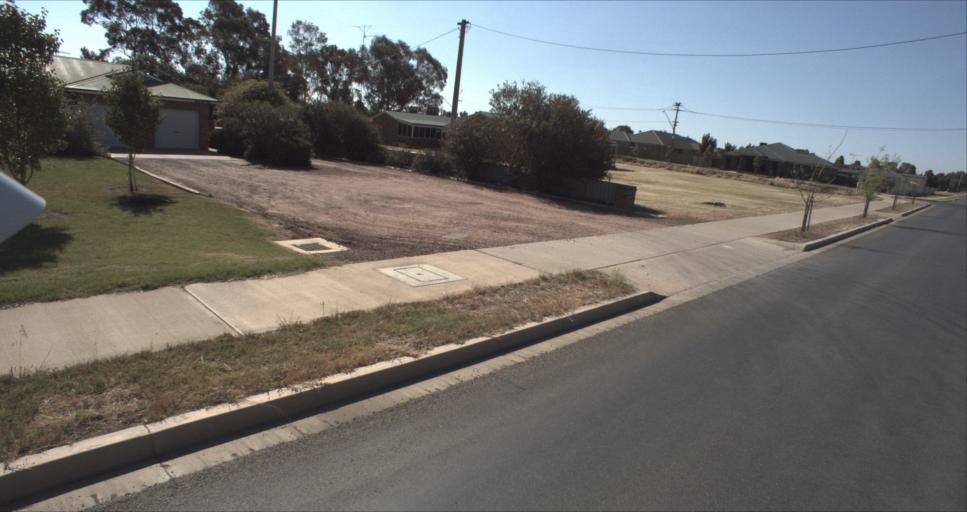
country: AU
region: New South Wales
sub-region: Leeton
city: Leeton
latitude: -34.5511
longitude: 146.4171
